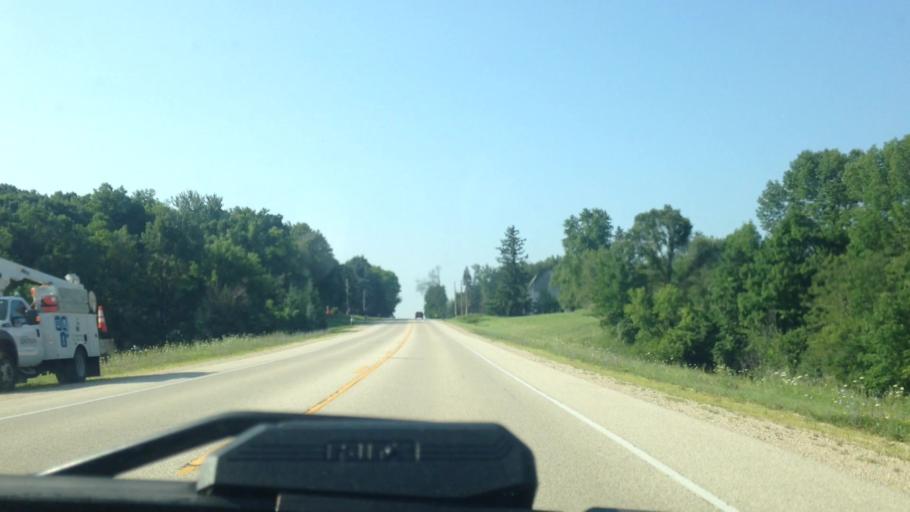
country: US
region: Wisconsin
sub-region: Washington County
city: Slinger
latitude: 43.3068
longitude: -88.2608
